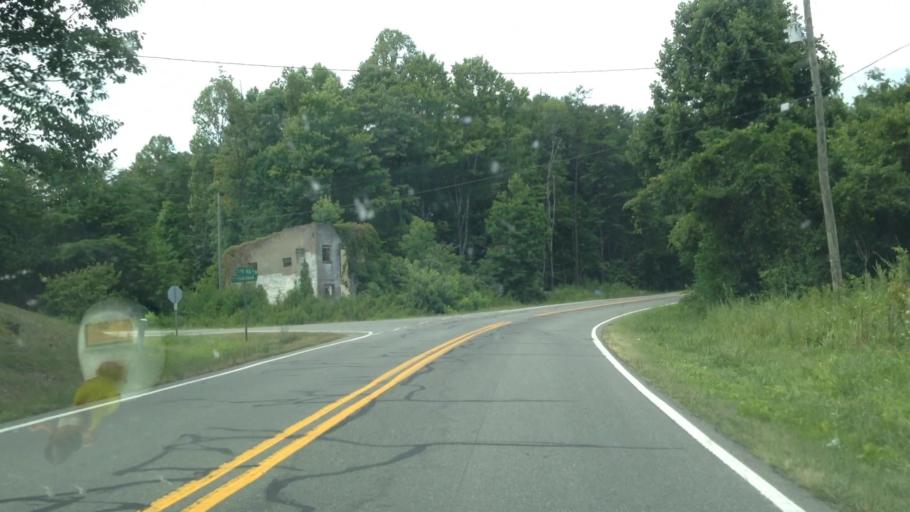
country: US
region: North Carolina
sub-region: Stokes County
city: Walnut Cove
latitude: 36.2597
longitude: -80.0999
